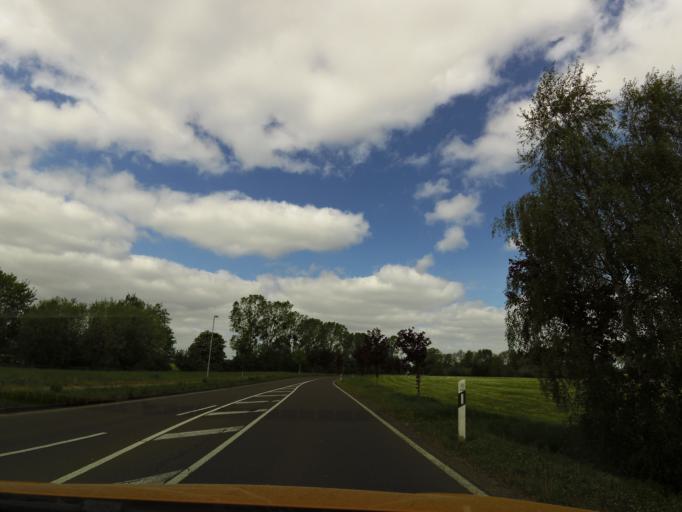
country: DE
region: Saxony-Anhalt
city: Mockern
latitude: 52.1941
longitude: 11.9052
